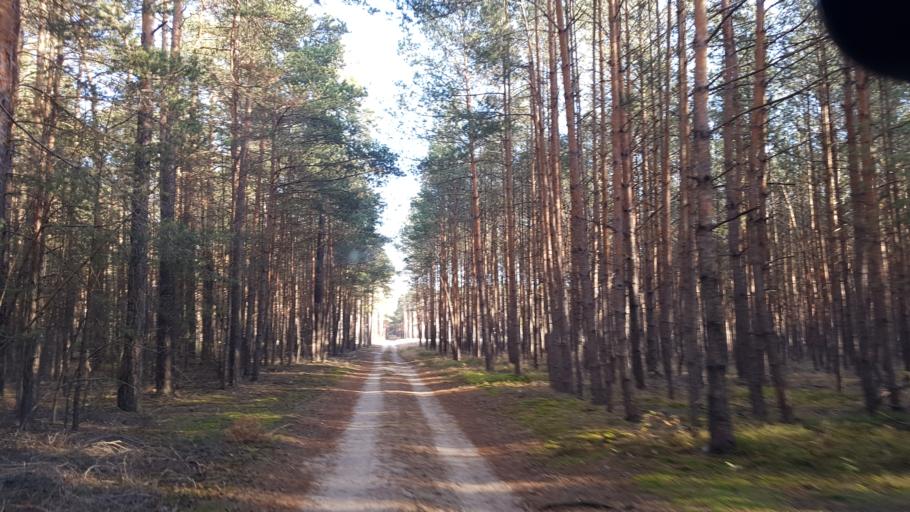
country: DE
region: Brandenburg
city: Schonewalde
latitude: 51.6493
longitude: 13.6314
